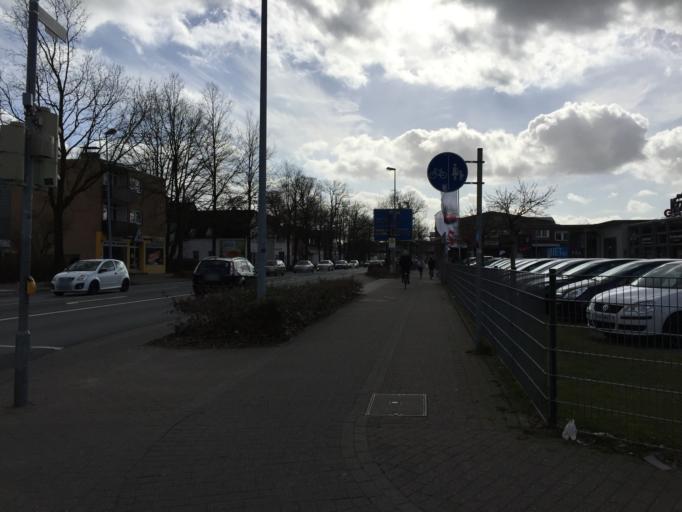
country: DE
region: Lower Saxony
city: Oldenburg
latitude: 53.1662
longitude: 8.2267
